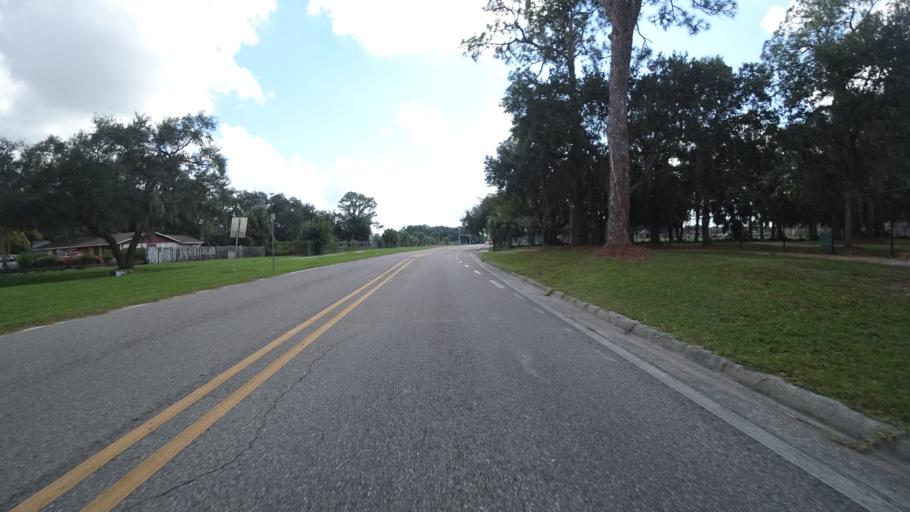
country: US
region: Florida
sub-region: Manatee County
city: Whitfield
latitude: 27.4316
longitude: -82.5553
